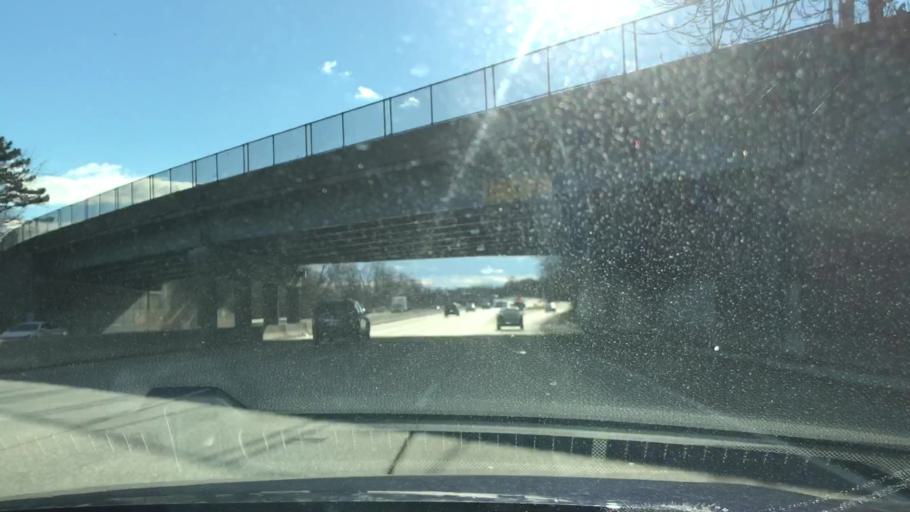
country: US
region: New Jersey
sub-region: Bergen County
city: Wallington
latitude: 40.8443
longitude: -74.1230
